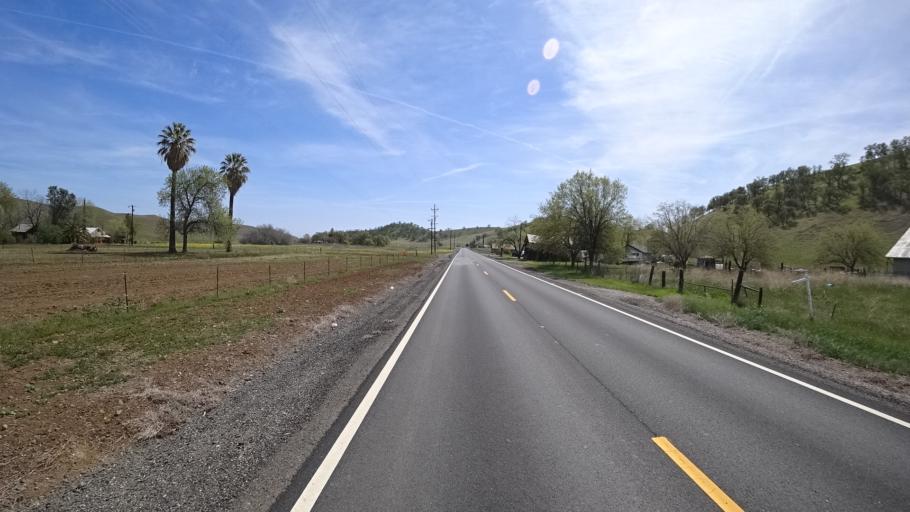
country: US
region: California
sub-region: Glenn County
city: Willows
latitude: 39.5892
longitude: -122.4519
